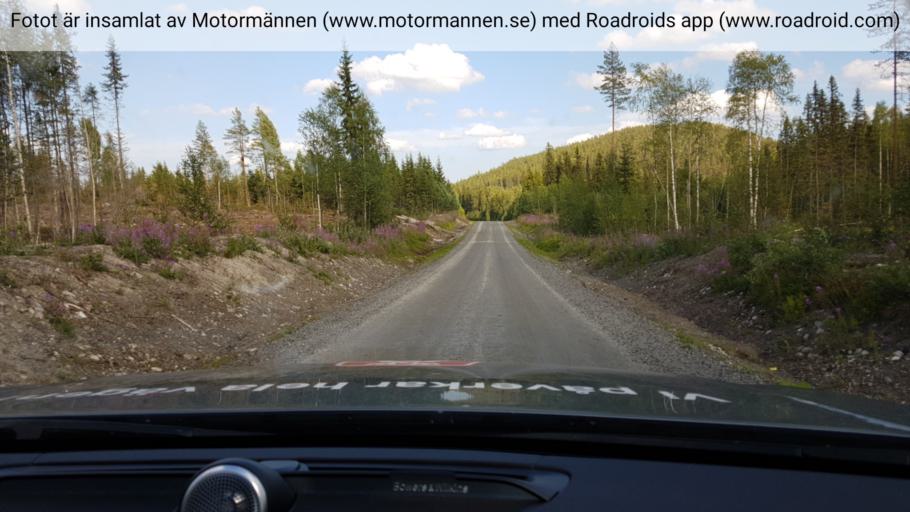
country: SE
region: Vaesterbotten
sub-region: Dorotea Kommun
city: Dorotea
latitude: 63.9193
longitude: 16.2112
